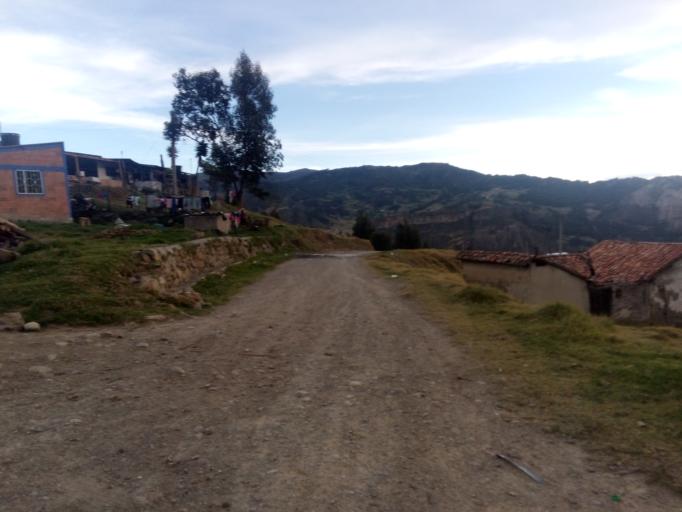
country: CO
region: Boyaca
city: Gameza
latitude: 5.8033
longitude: -72.8017
